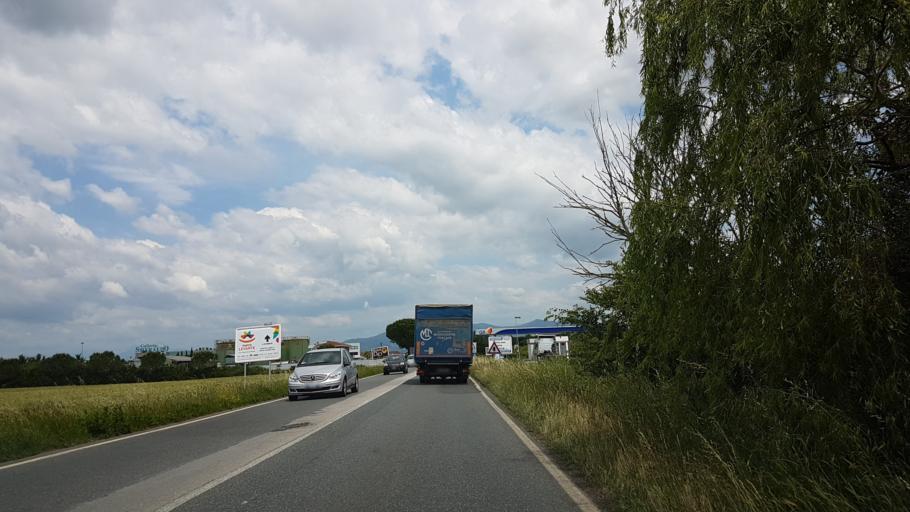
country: IT
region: Tuscany
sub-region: Provincia di Livorno
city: Collesalvetti
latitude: 43.5909
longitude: 10.4715
